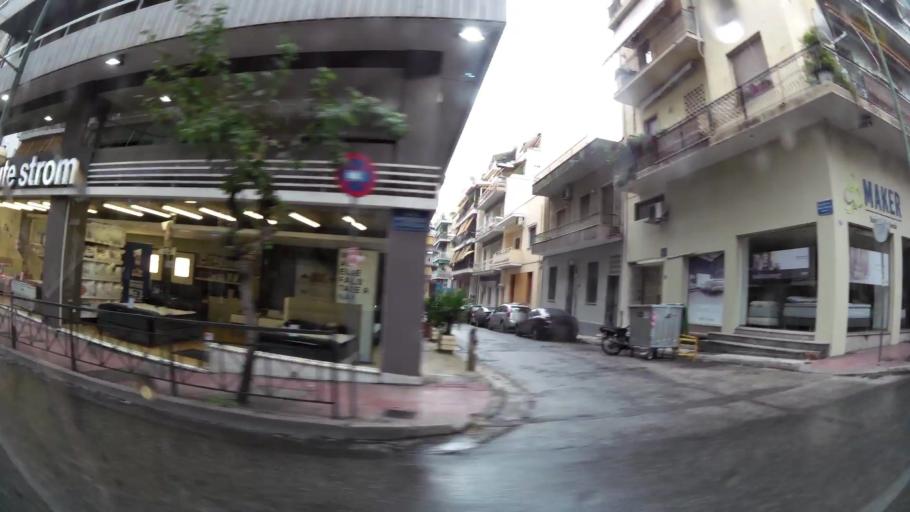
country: GR
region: Attica
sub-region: Nomarchia Athinas
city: Dhafni
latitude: 37.9582
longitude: 23.7381
